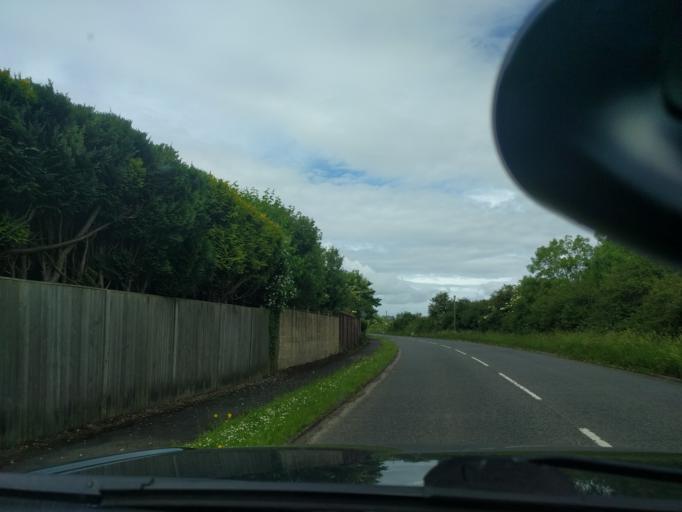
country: GB
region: England
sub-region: Wiltshire
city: Westwood
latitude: 51.3515
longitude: -2.2827
